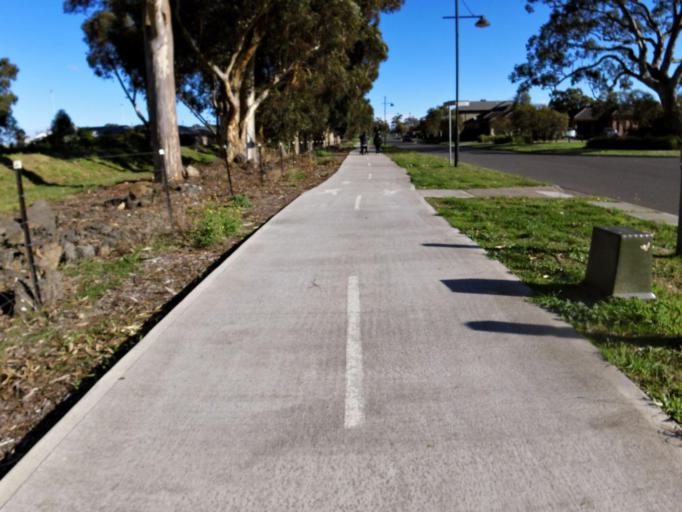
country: AU
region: Victoria
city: Plenty
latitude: -37.6392
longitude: 145.0917
